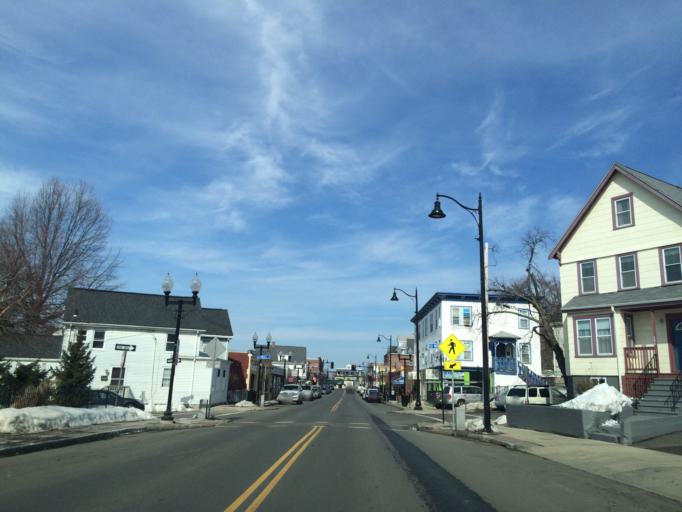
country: US
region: Massachusetts
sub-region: Middlesex County
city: Somerville
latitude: 42.3954
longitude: -71.1029
